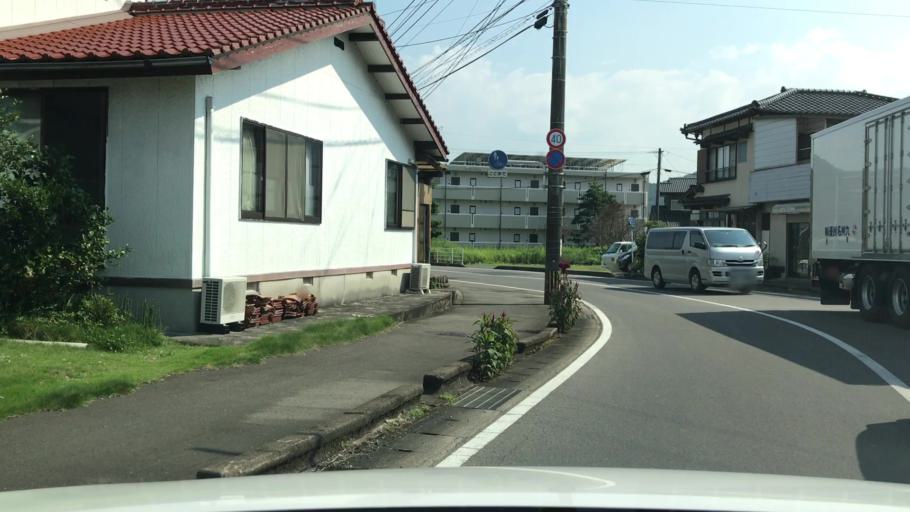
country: JP
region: Saga Prefecture
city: Kashima
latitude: 33.1255
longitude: 130.0622
